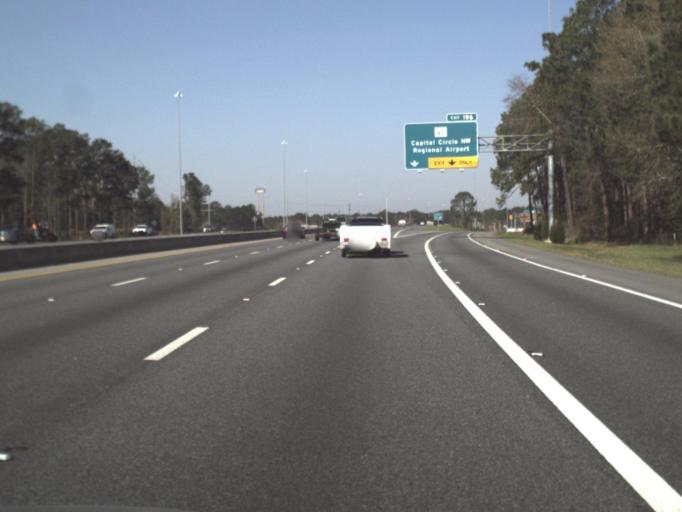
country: US
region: Florida
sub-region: Leon County
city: Tallahassee
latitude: 30.4787
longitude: -84.3572
